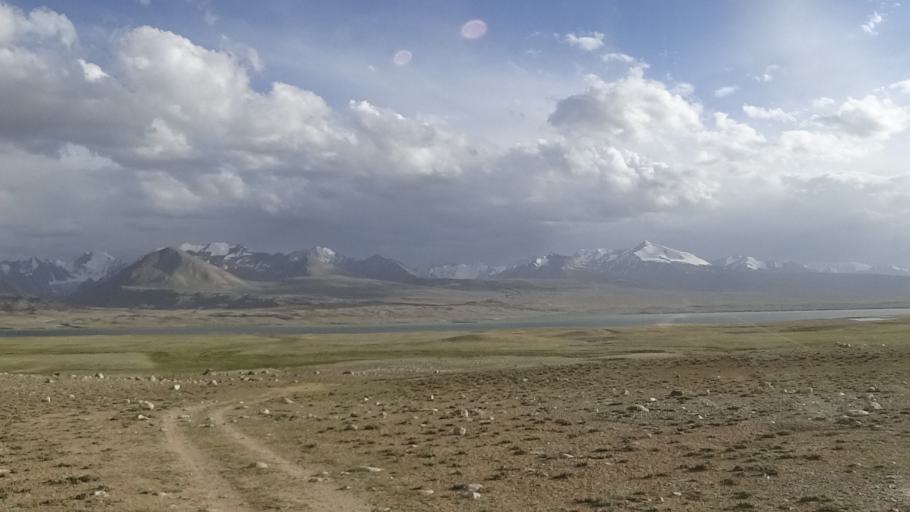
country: TJ
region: Gorno-Badakhshan
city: Murghob
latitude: 37.4654
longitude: 73.6132
